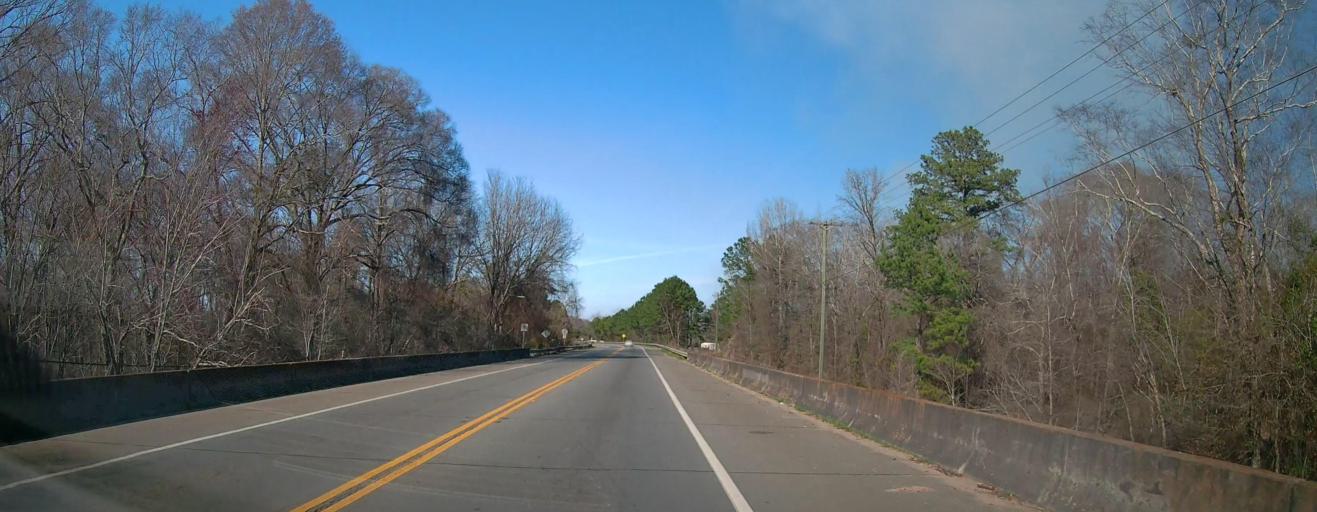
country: US
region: Georgia
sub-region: Macon County
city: Oglethorpe
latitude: 32.3111
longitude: -84.0651
